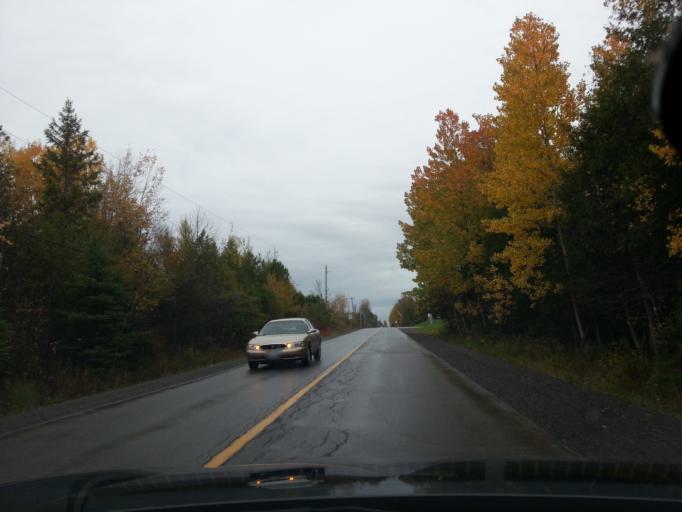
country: CA
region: Ontario
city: Bells Corners
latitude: 45.2360
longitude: -75.9312
